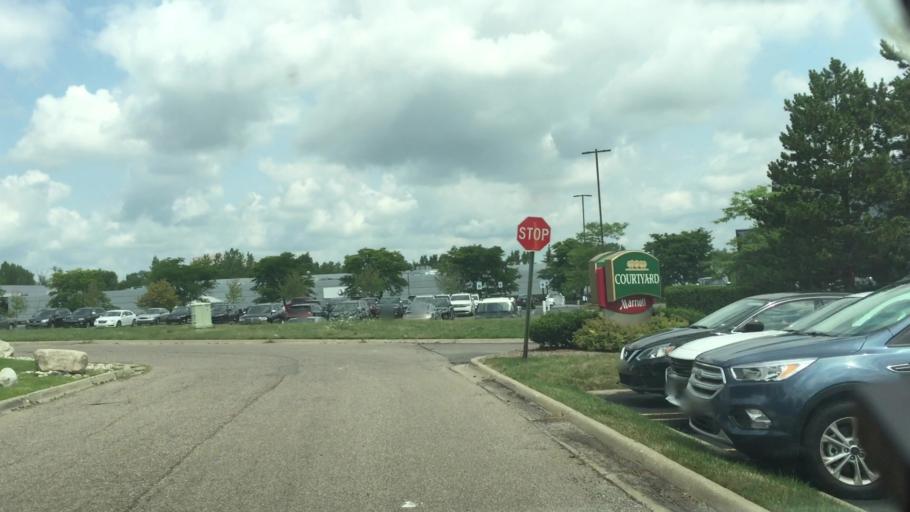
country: US
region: Michigan
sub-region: Oakland County
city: Auburn Hills
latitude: 42.6589
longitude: -83.2424
